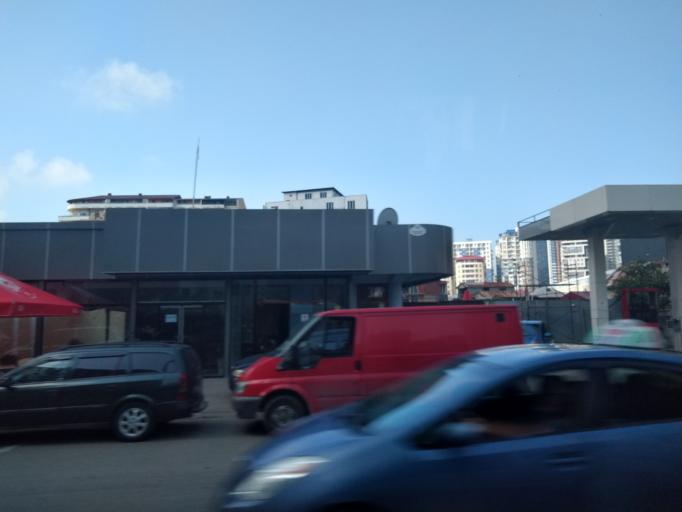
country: GE
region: Ajaria
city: Batumi
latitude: 41.6333
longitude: 41.6109
